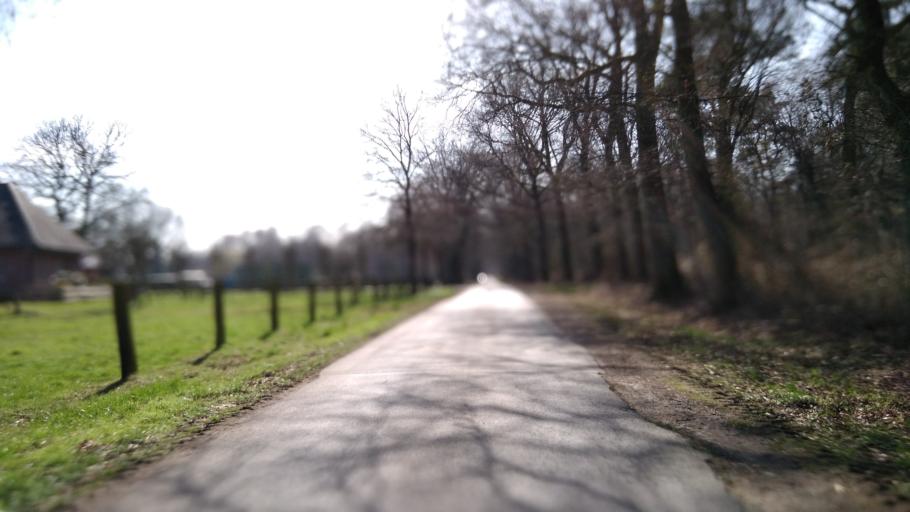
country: DE
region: North Rhine-Westphalia
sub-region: Regierungsbezirk Munster
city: Gladbeck
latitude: 51.5877
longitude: 6.9278
